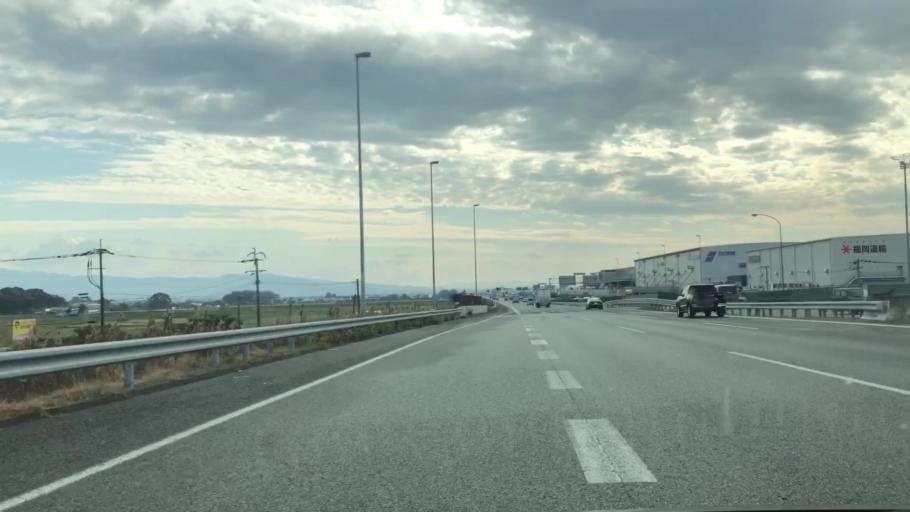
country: JP
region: Saga Prefecture
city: Tosu
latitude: 33.3928
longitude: 130.5384
